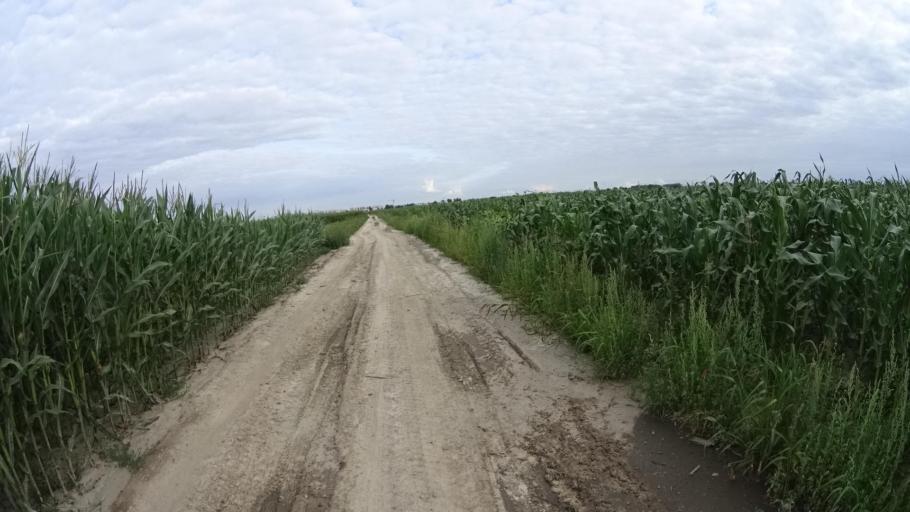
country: PL
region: Masovian Voivodeship
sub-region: Powiat warszawski zachodni
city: Babice
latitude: 52.2368
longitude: 20.8698
